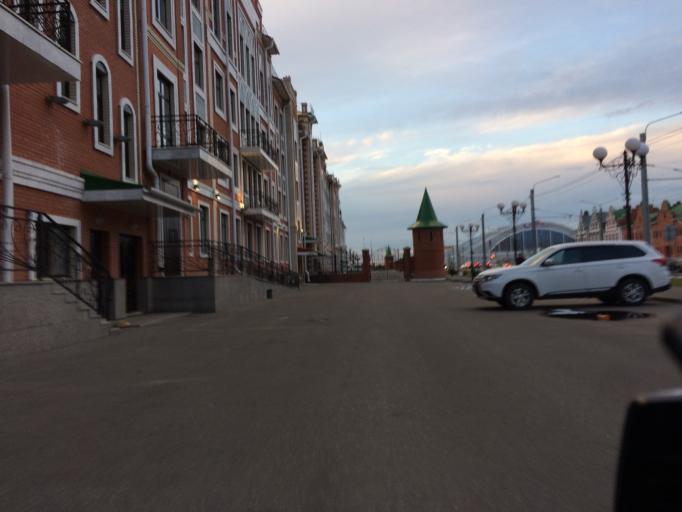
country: RU
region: Mariy-El
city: Yoshkar-Ola
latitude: 56.6353
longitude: 47.9112
